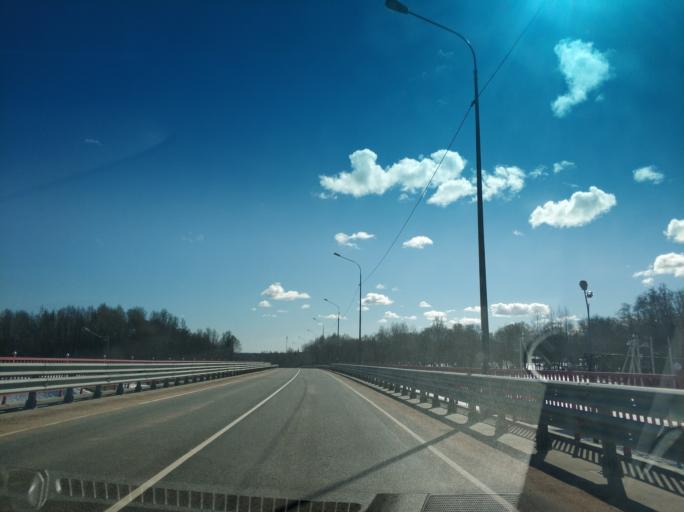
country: RU
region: Leningrad
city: Sosnovo
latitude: 60.4338
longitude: 30.2361
